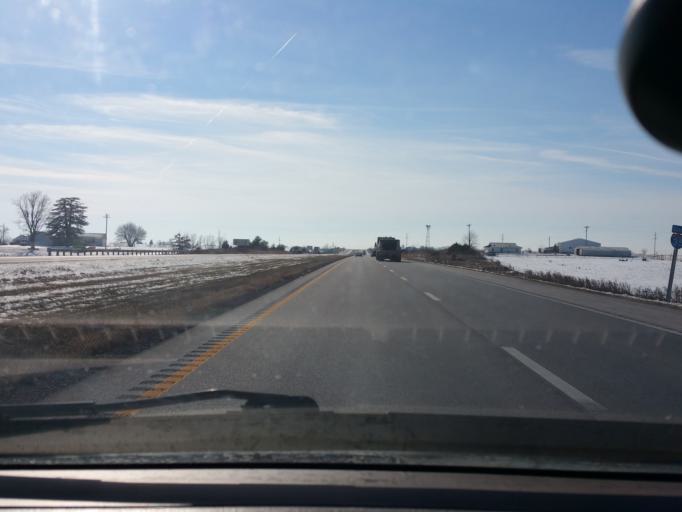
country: US
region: Missouri
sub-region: Clinton County
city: Cameron
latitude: 39.8486
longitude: -94.1791
